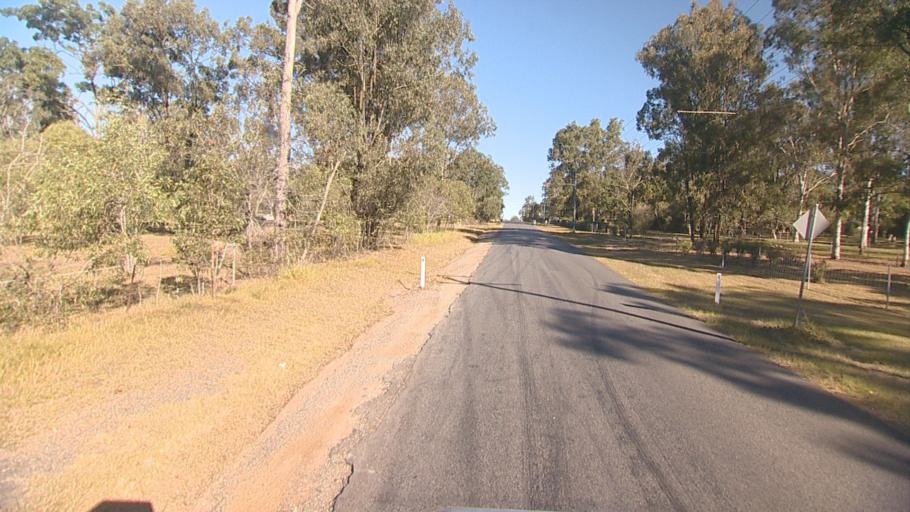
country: AU
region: Queensland
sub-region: Logan
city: Park Ridge South
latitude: -27.7242
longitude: 153.0206
